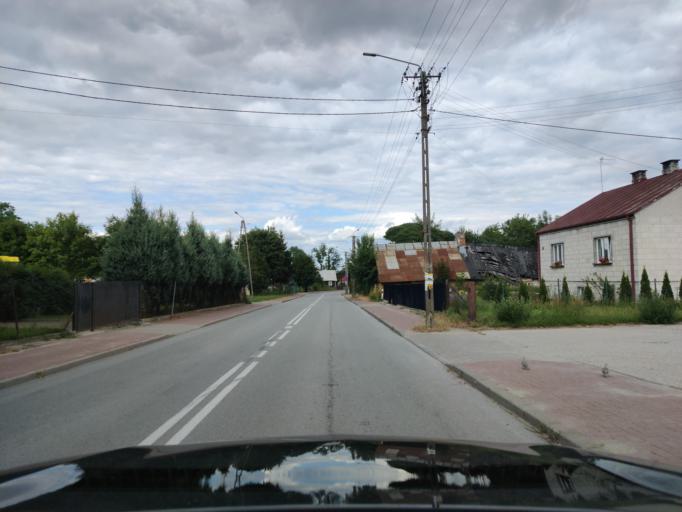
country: PL
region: Masovian Voivodeship
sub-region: Powiat sokolowski
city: Ceranow
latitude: 52.6278
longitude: 22.2239
